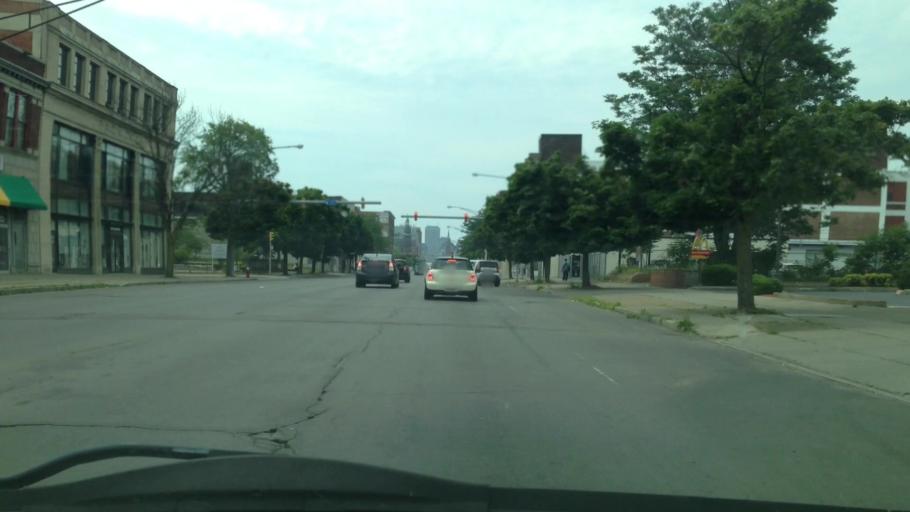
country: US
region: New York
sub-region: Erie County
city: Buffalo
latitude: 42.9103
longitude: -78.8663
